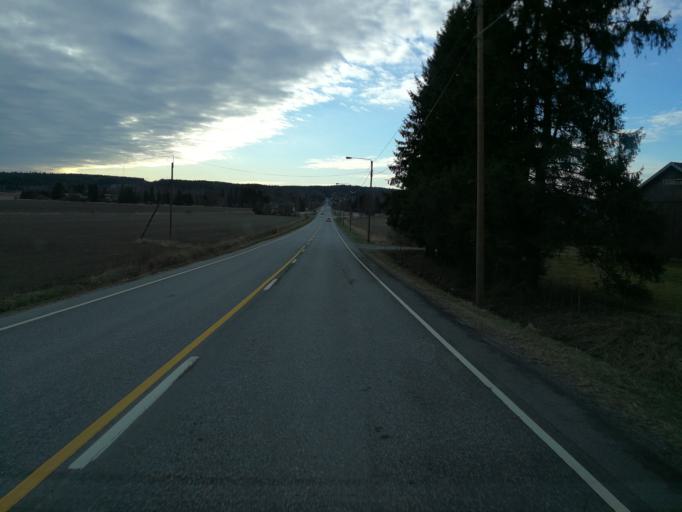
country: FI
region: Varsinais-Suomi
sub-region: Turku
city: Paimio
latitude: 60.4231
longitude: 22.6445
